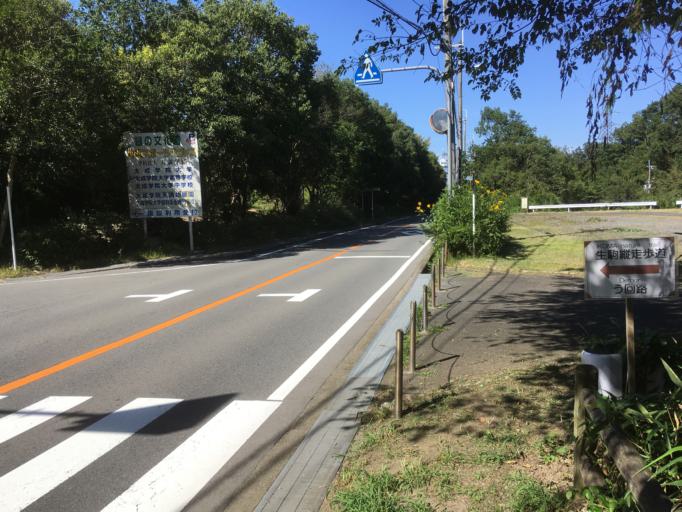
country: JP
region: Osaka
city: Daitocho
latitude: 34.7296
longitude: 135.6716
